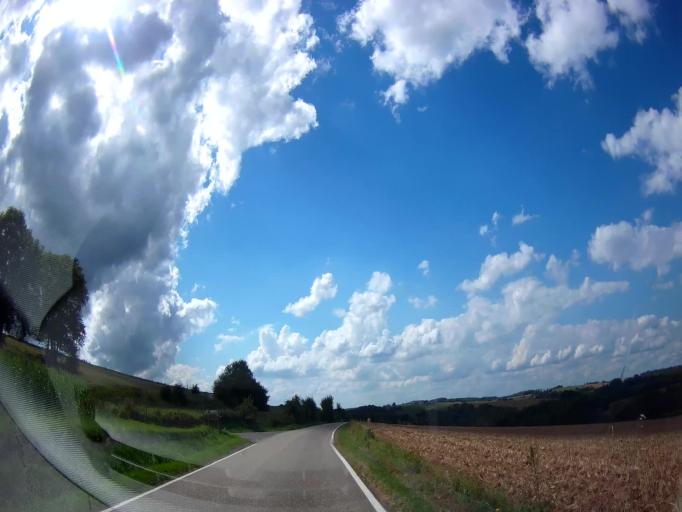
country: BE
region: Wallonia
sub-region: Province de Namur
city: Assesse
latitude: 50.3543
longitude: 4.9787
